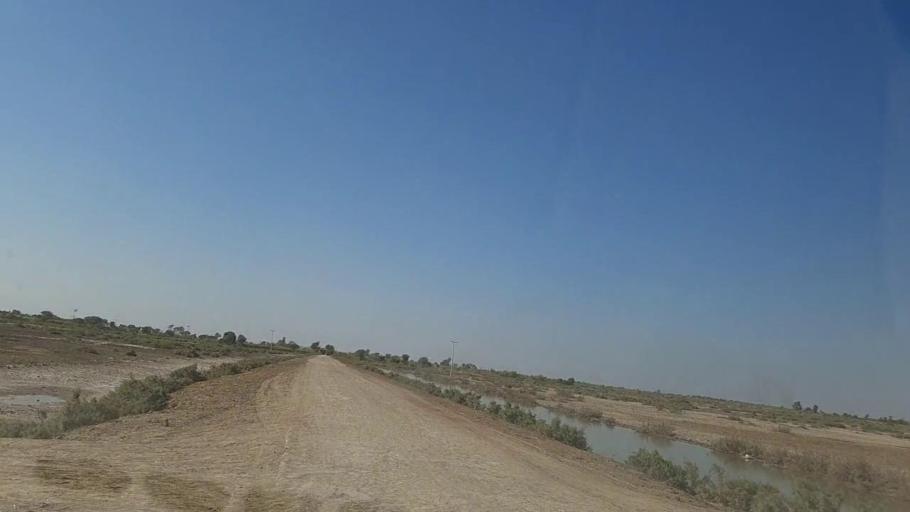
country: PK
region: Sindh
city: Digri
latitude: 25.1880
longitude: 68.9999
